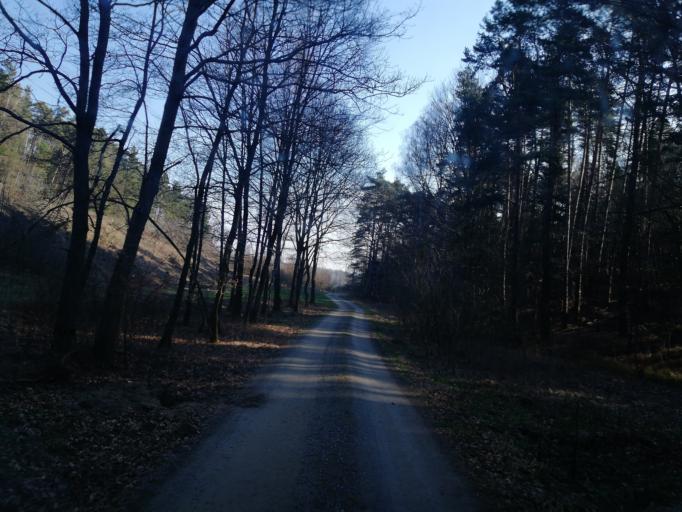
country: DE
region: Brandenburg
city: Drahnsdorf
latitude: 51.8351
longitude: 13.5971
